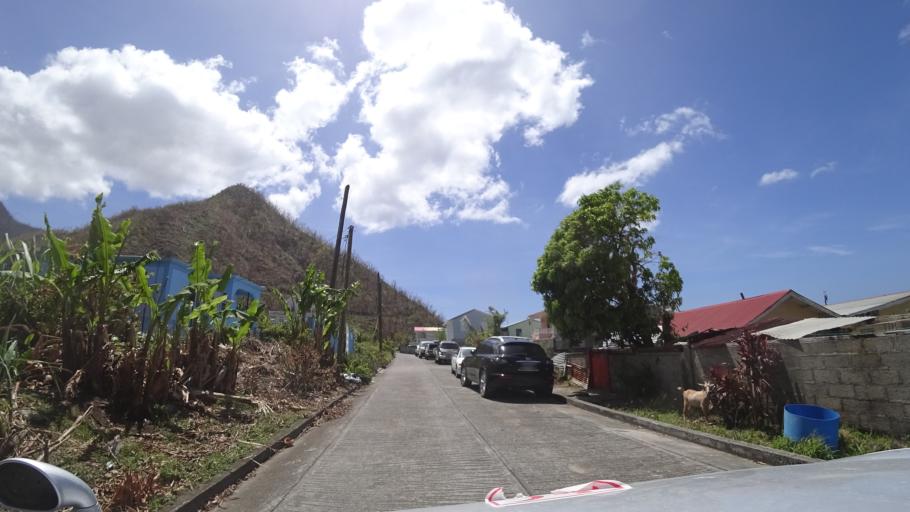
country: DM
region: Saint Luke
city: Pointe Michel
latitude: 15.2607
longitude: -61.3754
